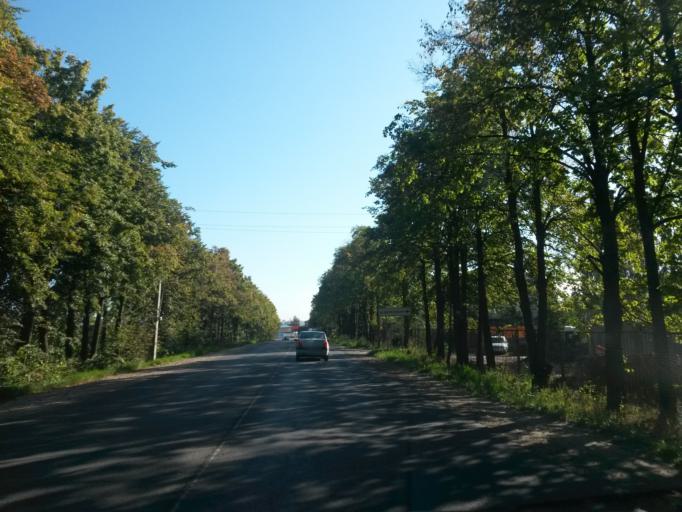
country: RU
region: Moscow
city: Zyablikovo
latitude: 55.5999
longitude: 37.7913
